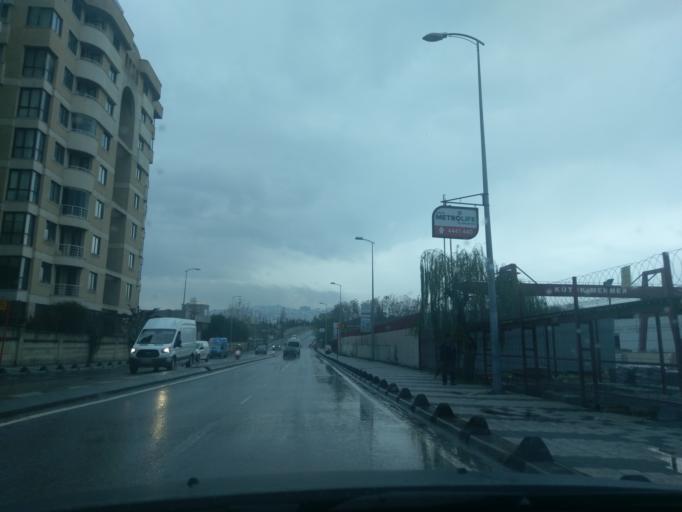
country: TR
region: Istanbul
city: Sancaktepe
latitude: 41.0255
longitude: 29.2367
